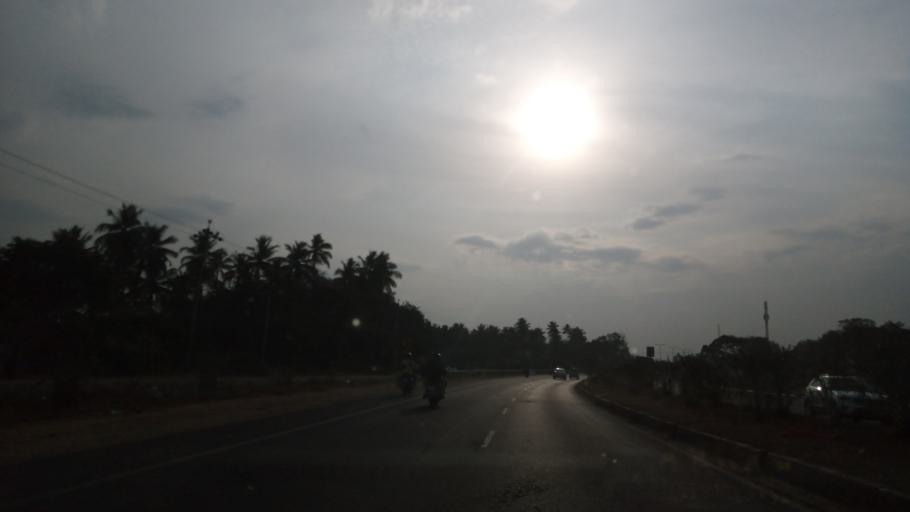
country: IN
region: Tamil Nadu
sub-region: Salem
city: Salem
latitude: 11.6649
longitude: 78.2884
